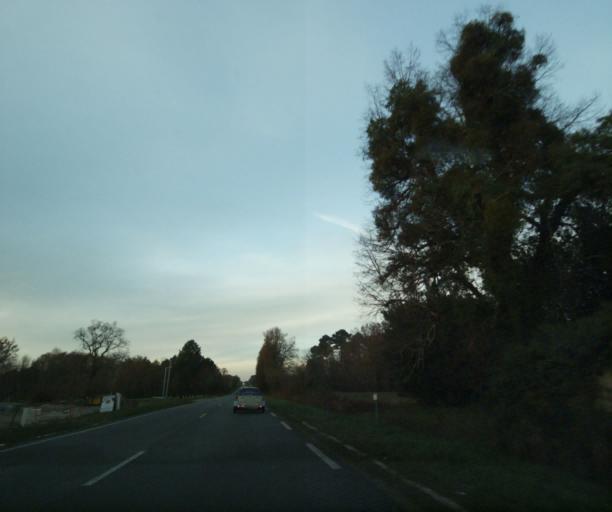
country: FR
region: Aquitaine
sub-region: Departement de la Gironde
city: Bazas
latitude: 44.4861
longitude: -0.2322
